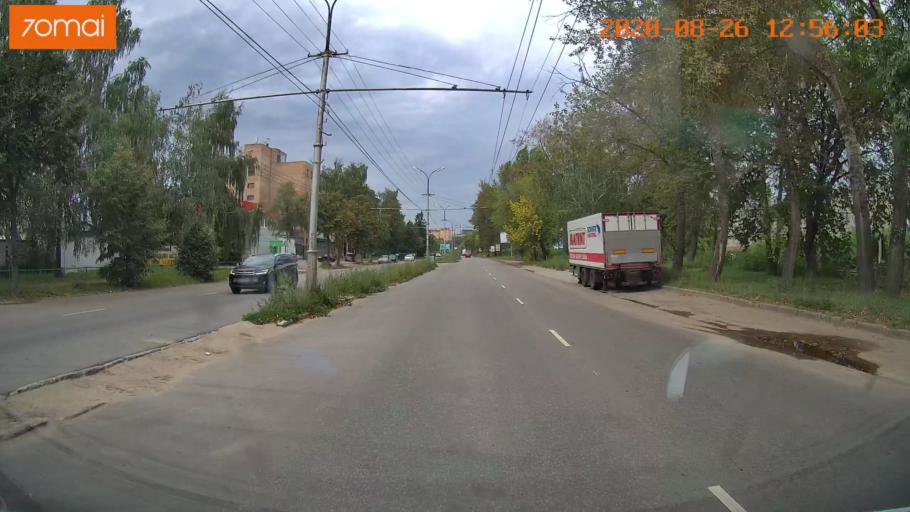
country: RU
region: Rjazan
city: Ryazan'
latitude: 54.6118
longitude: 39.7543
